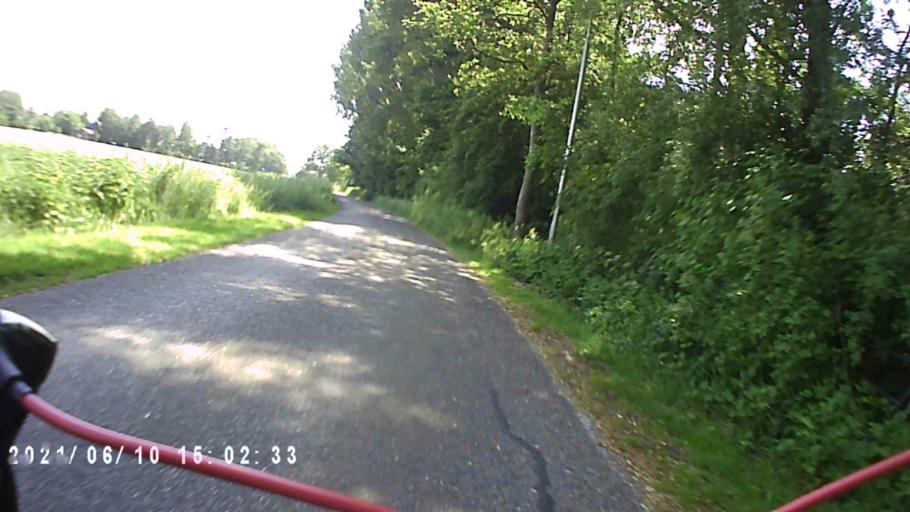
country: NL
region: Groningen
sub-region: Gemeente Grootegast
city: Grootegast
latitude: 53.2001
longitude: 6.2310
